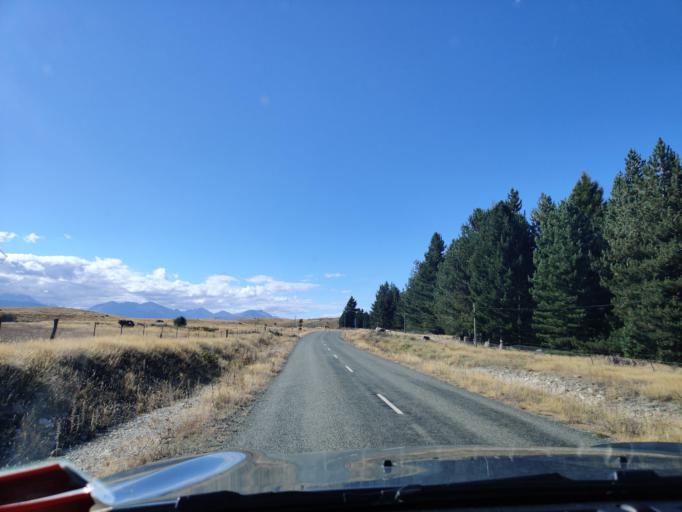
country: NZ
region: Canterbury
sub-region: Timaru District
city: Pleasant Point
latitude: -43.9977
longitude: 170.4508
